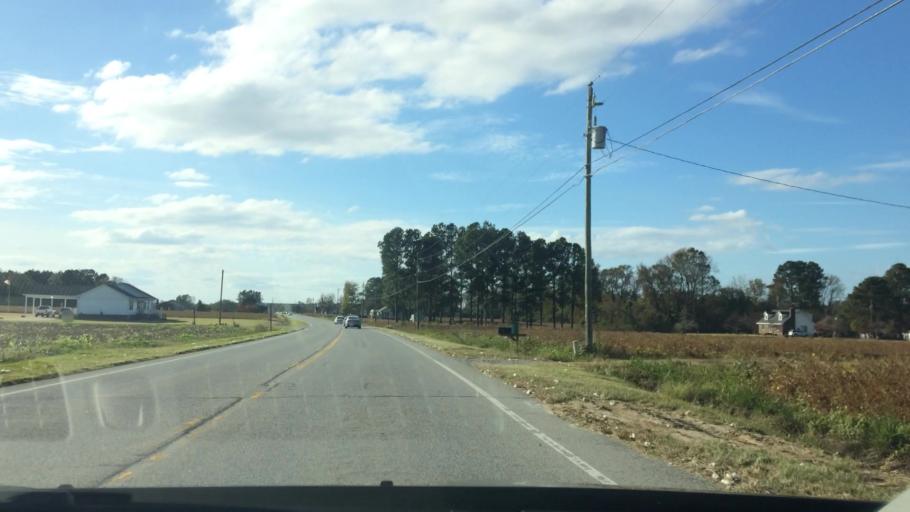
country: US
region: North Carolina
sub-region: Greene County
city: Snow Hill
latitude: 35.4414
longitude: -77.7972
